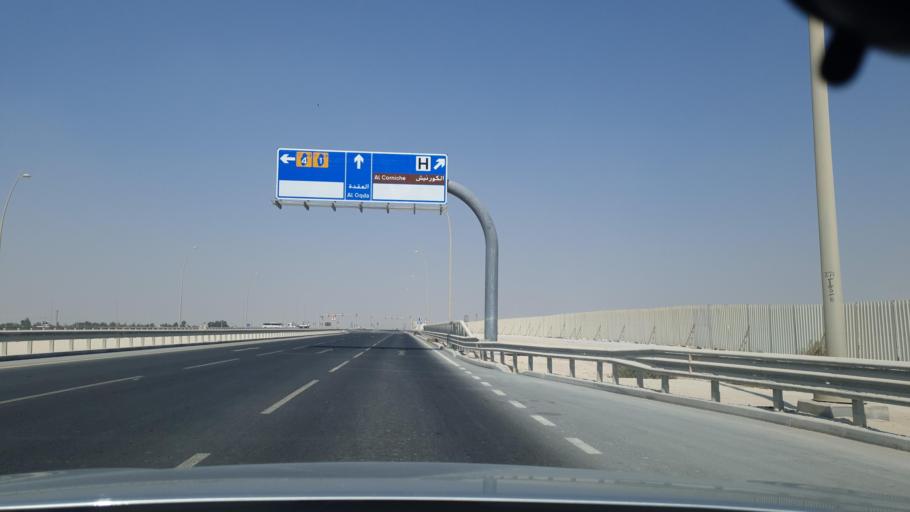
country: QA
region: Al Khawr
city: Al Khawr
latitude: 25.6633
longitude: 51.4782
